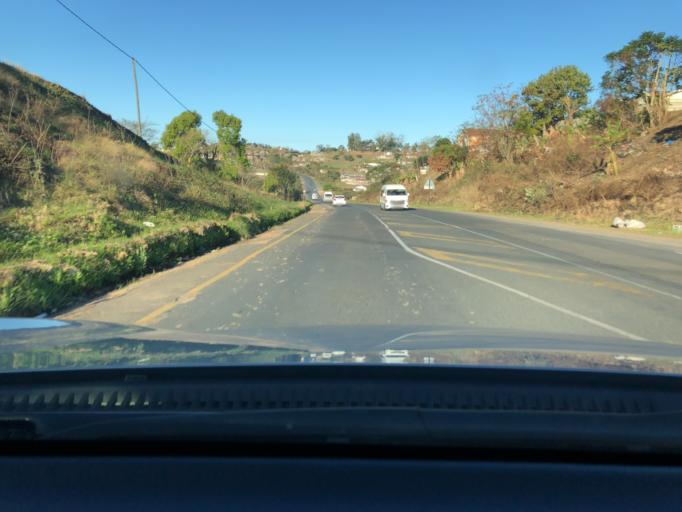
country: ZA
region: KwaZulu-Natal
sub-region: eThekwini Metropolitan Municipality
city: Umkomaas
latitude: -30.0356
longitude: 30.8153
